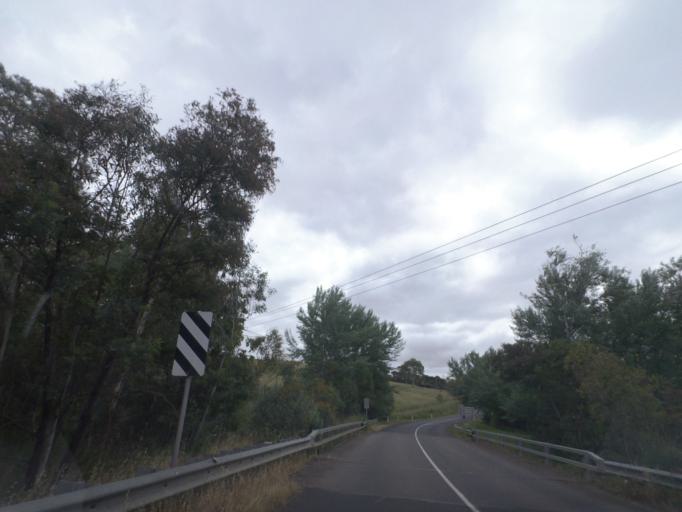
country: AU
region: Victoria
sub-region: Whittlesea
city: Whittlesea
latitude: -37.1986
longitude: 145.0384
